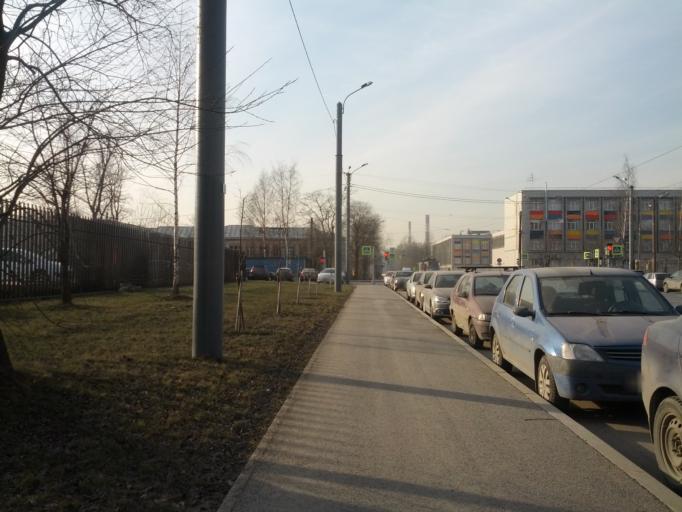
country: RU
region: Leningrad
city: Kalininskiy
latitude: 59.9632
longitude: 30.3998
